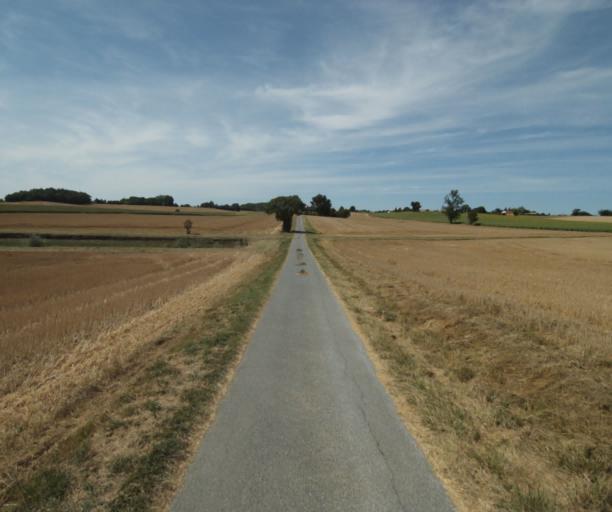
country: FR
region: Midi-Pyrenees
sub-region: Departement du Tarn
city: Puylaurens
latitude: 43.5261
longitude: 2.0194
